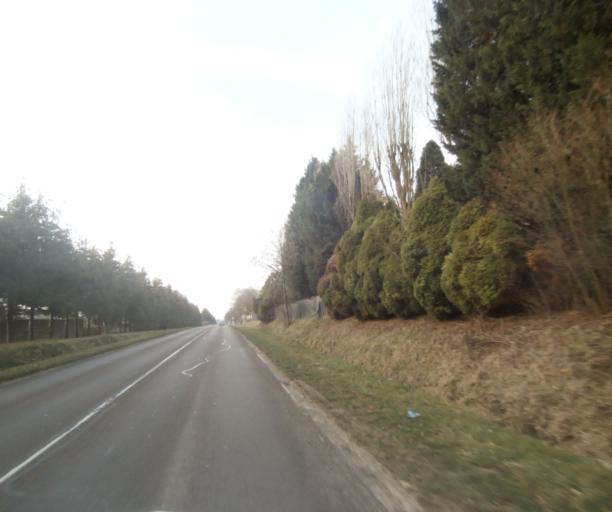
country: FR
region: Champagne-Ardenne
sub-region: Departement de la Haute-Marne
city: Chancenay
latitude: 48.6622
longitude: 4.9757
